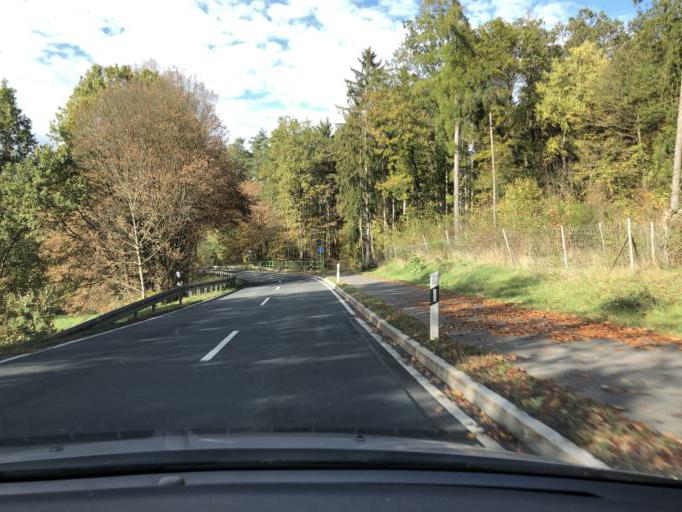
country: DE
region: Thuringia
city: Schleusingen
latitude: 50.4969
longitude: 10.7788
